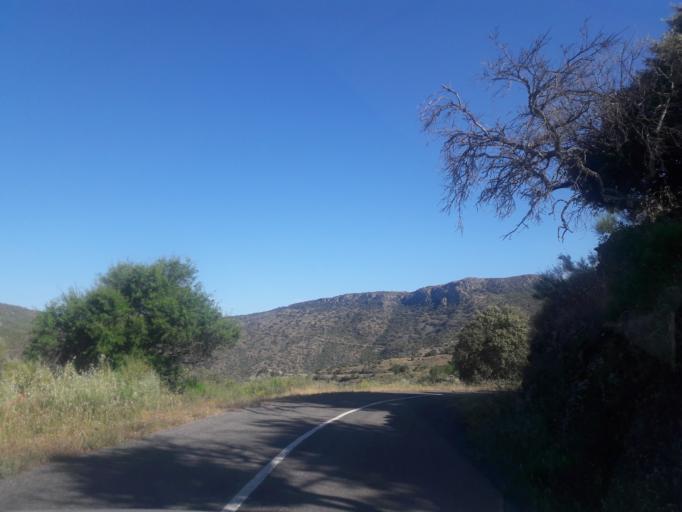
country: ES
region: Castille and Leon
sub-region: Provincia de Salamanca
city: Saucelle
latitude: 41.0157
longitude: -6.7485
